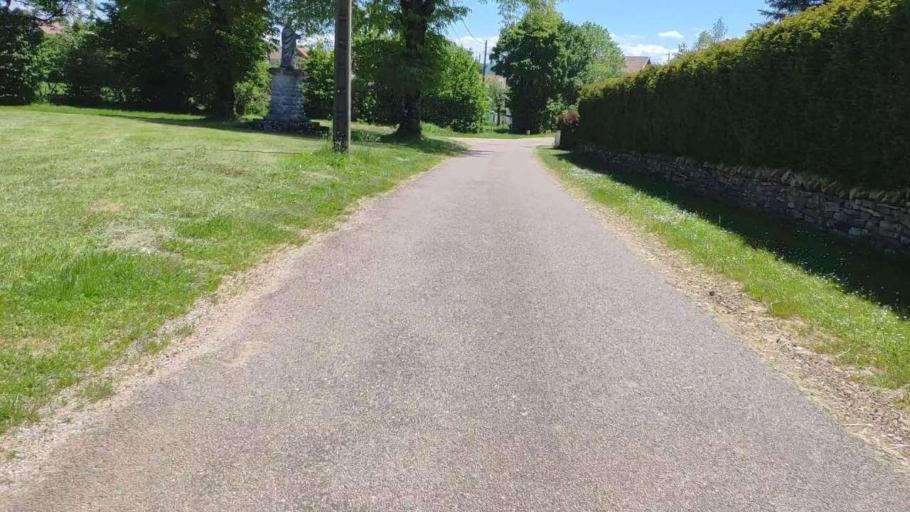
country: FR
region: Franche-Comte
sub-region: Departement du Jura
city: Poligny
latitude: 46.7363
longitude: 5.6945
